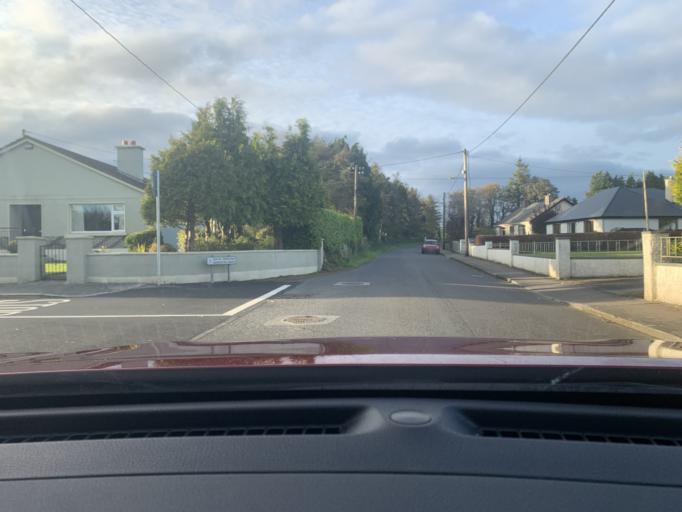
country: IE
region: Connaught
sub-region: Roscommon
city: Ballaghaderreen
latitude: 53.9051
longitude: -8.5770
